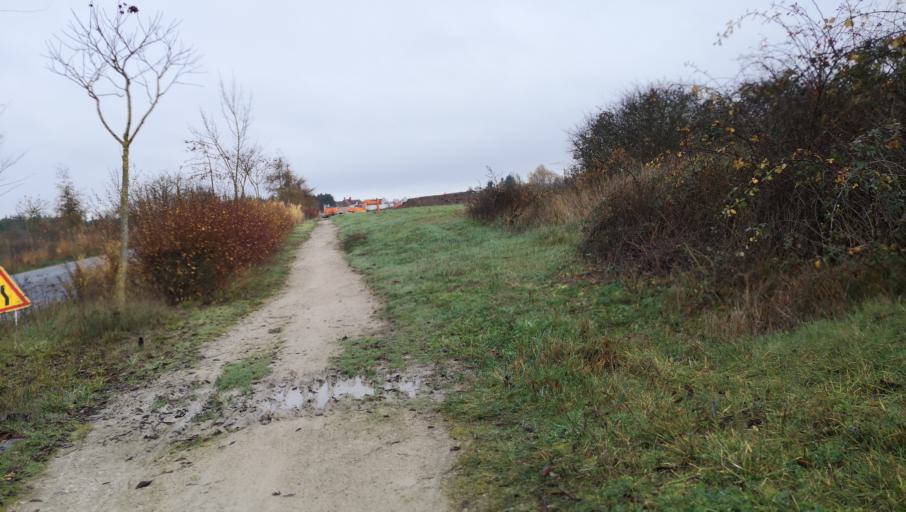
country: FR
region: Centre
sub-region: Departement du Loiret
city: Marigny-les-Usages
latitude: 47.9458
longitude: 2.0096
